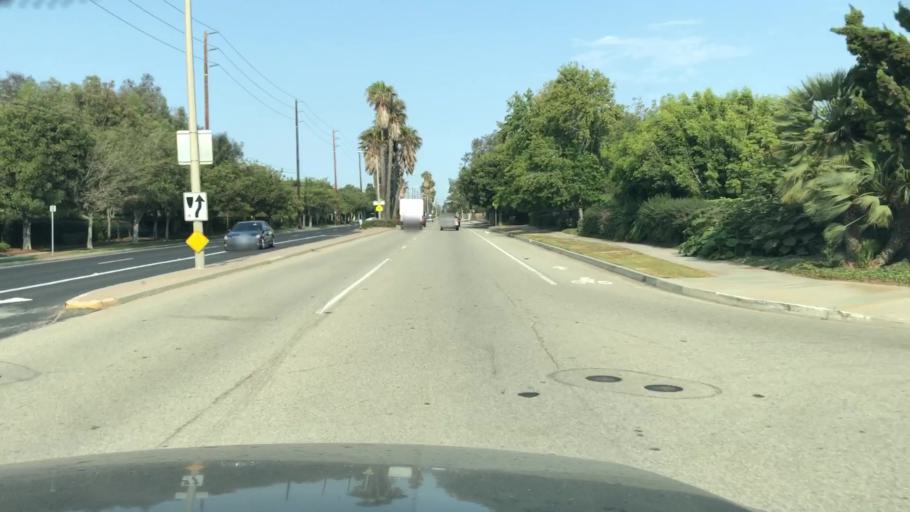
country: US
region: California
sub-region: Ventura County
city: Oxnard
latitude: 34.2193
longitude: -119.2047
